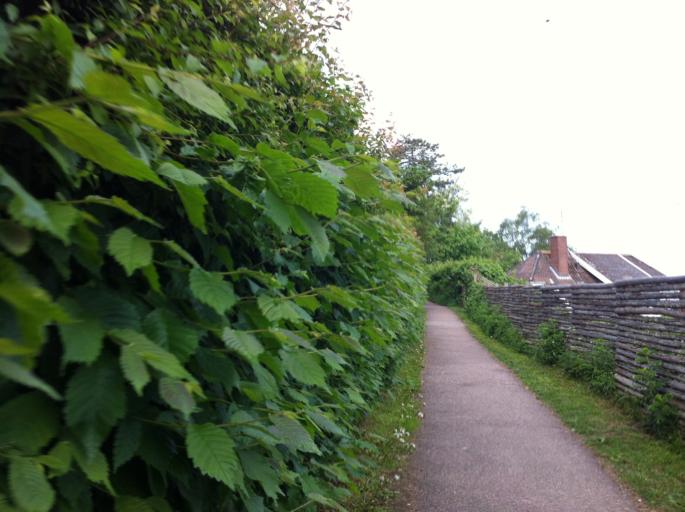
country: DK
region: Capital Region
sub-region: Gribskov Kommune
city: Gilleleje
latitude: 56.1266
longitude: 12.2954
